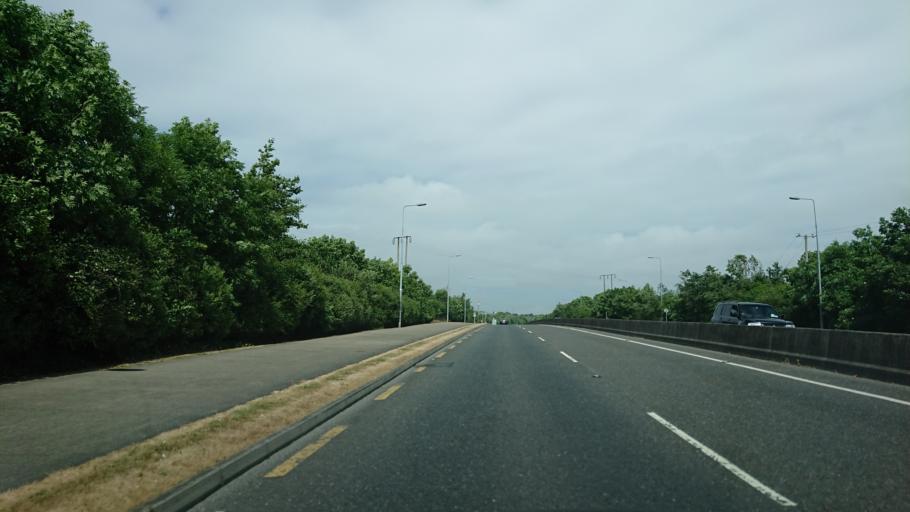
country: IE
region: Munster
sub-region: Waterford
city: Waterford
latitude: 52.2302
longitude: -7.1110
